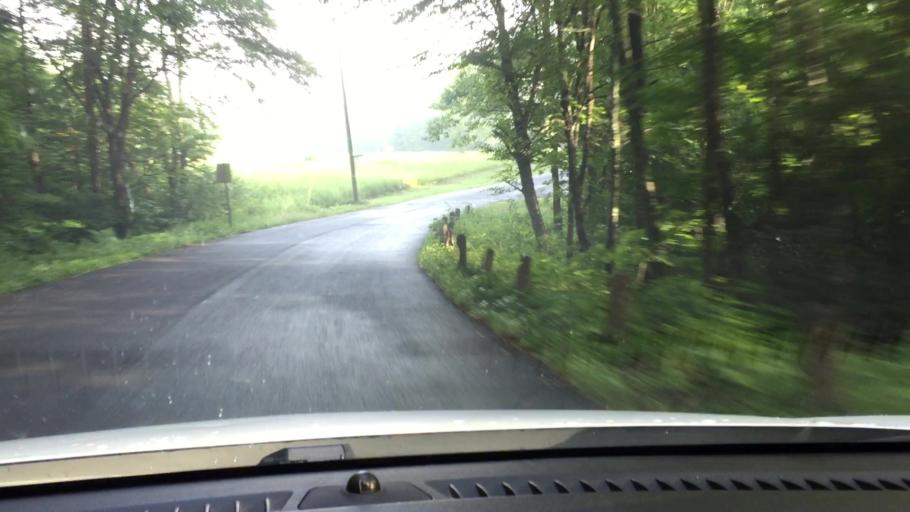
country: US
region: Massachusetts
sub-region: Hampshire County
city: Chesterfield
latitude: 42.3435
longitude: -72.9537
